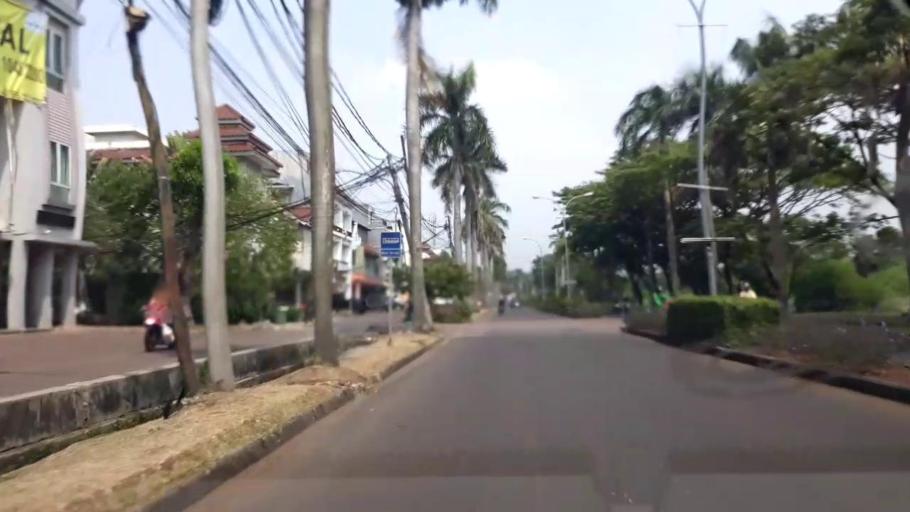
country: ID
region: Banten
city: Curug
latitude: -6.2241
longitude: 106.5914
